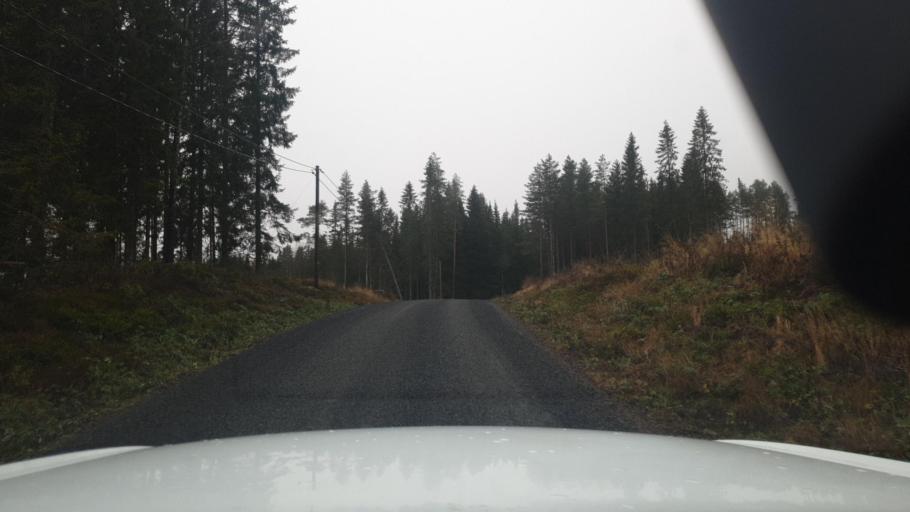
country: SE
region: Vaermland
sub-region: Eda Kommun
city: Charlottenberg
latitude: 60.1471
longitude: 12.5959
